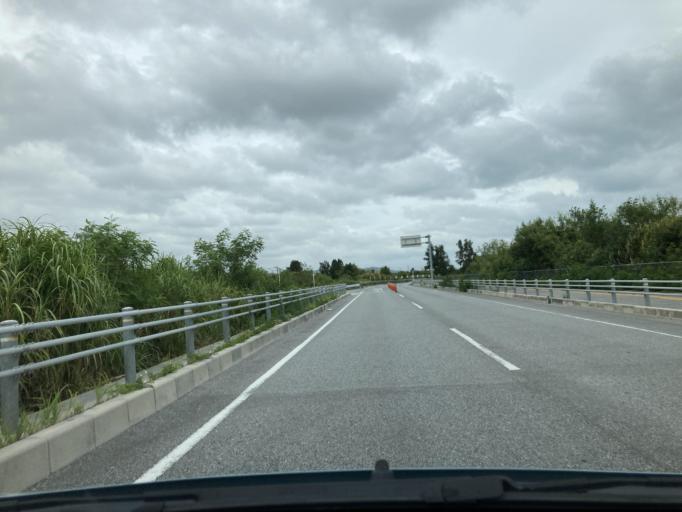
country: JP
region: Okinawa
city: Ginowan
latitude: 26.2164
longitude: 127.7724
